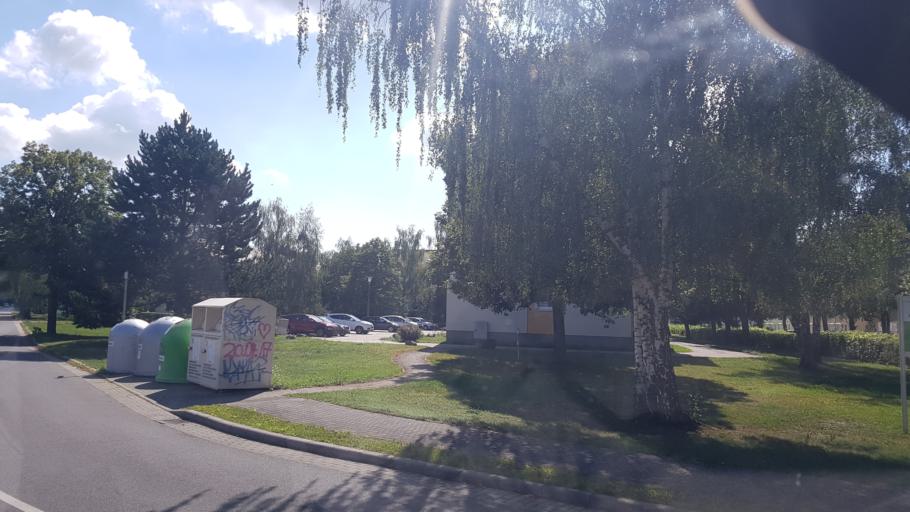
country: DE
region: Brandenburg
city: Drebkau
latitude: 51.6537
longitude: 14.2296
